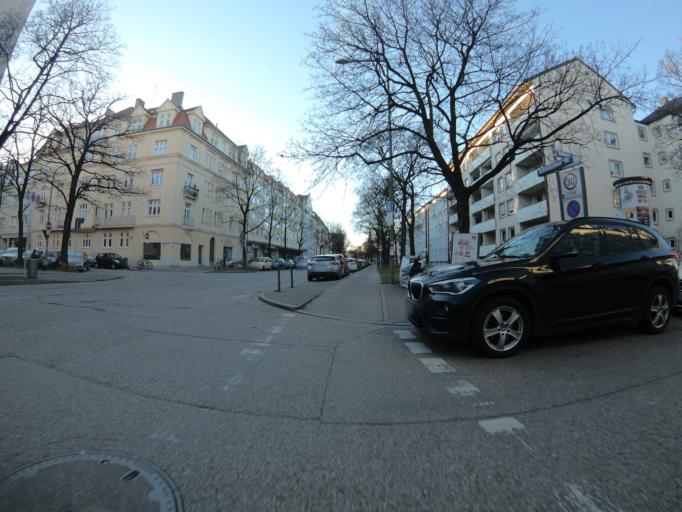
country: DE
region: Bavaria
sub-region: Upper Bavaria
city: Munich
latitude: 48.1131
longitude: 11.5863
